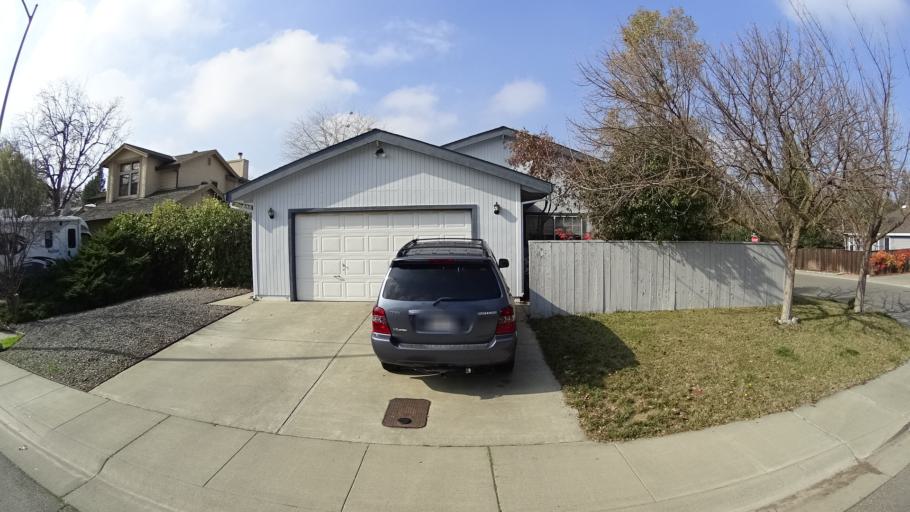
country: US
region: California
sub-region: Yolo County
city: Davis
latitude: 38.5721
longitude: -121.7551
